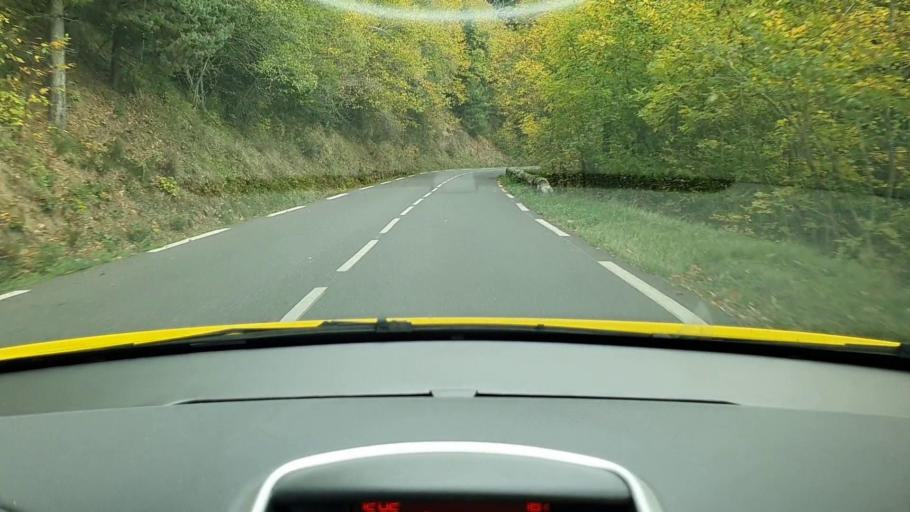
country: FR
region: Languedoc-Roussillon
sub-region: Departement de la Lozere
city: Meyrueis
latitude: 44.1295
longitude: 3.4180
